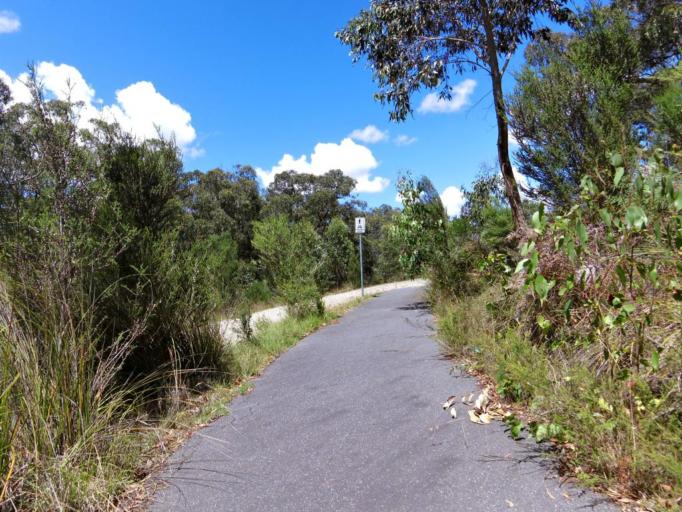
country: AU
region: Victoria
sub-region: Cardinia
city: Officer
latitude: -38.0314
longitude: 145.4278
